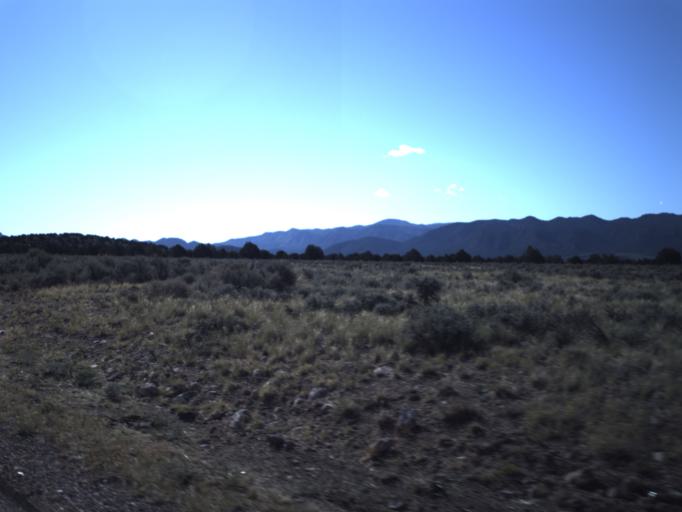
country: US
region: Utah
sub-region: Washington County
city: Enterprise
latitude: 37.6676
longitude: -113.4786
